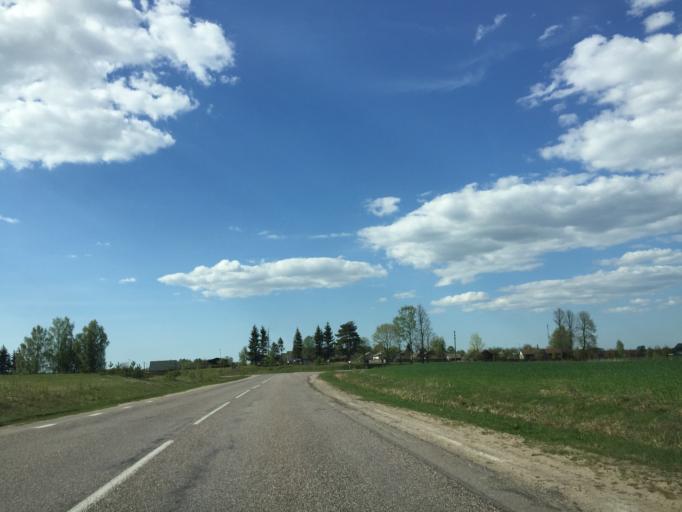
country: LV
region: Limbazu Rajons
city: Limbazi
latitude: 57.5125
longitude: 24.8147
